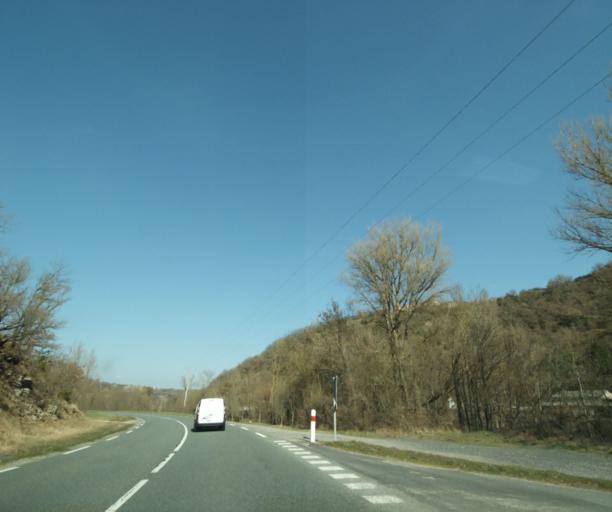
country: FR
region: Midi-Pyrenees
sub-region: Departement de l'Aveyron
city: Saint-Georges-de-Luzencon
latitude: 43.9993
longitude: 2.9697
